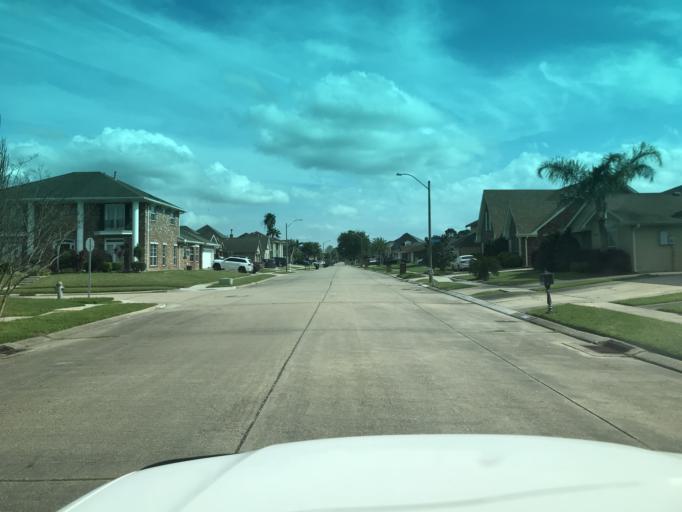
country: US
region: Louisiana
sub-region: Saint Bernard Parish
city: Chalmette
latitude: 30.0365
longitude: -89.9576
